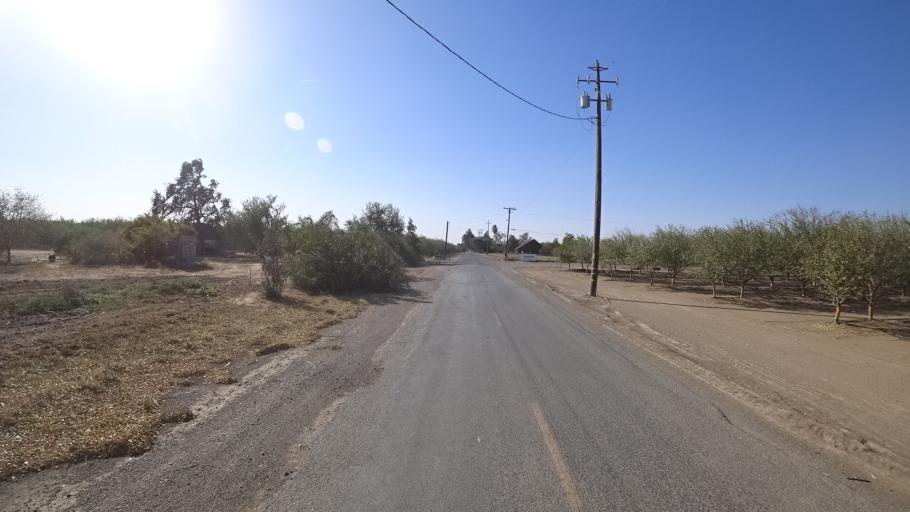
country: US
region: California
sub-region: Yolo County
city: Woodland
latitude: 38.7497
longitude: -121.7934
